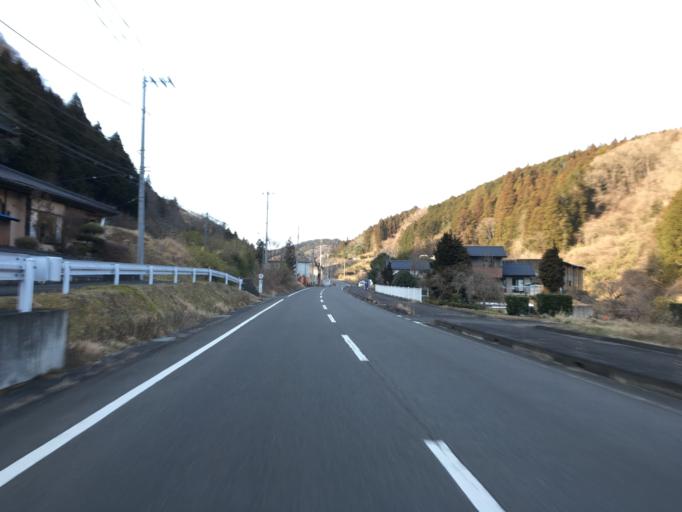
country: JP
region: Ibaraki
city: Daigo
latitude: 36.7300
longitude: 140.4587
